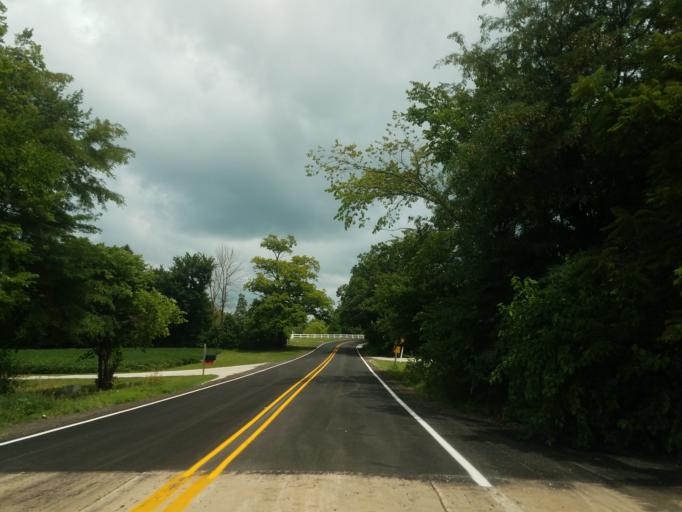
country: US
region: Illinois
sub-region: McLean County
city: Bloomington
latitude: 40.4531
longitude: -89.0383
